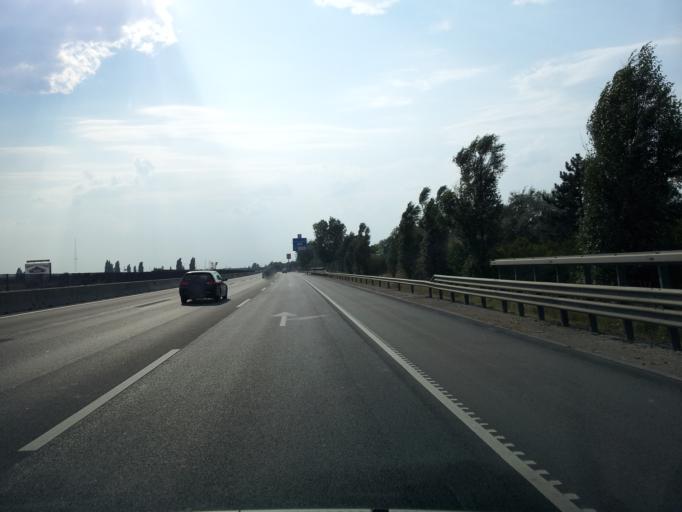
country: HU
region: Pest
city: Szigetszentmiklos
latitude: 47.3792
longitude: 19.0633
